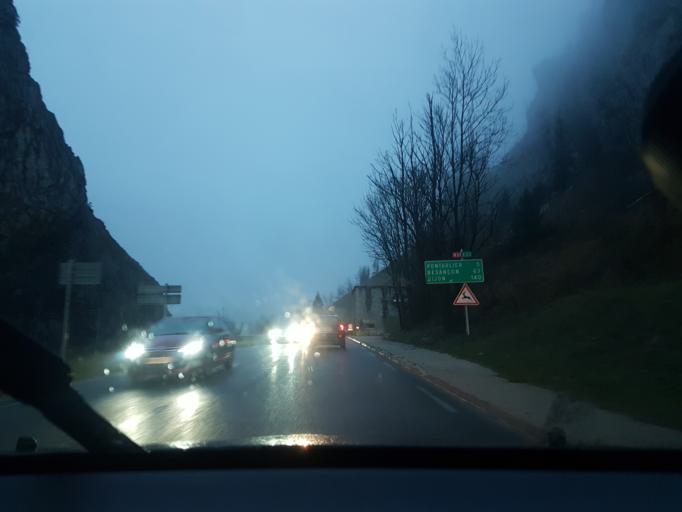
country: FR
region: Franche-Comte
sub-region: Departement du Doubs
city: La Cluse-et-Mijoux
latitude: 46.8738
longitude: 6.3769
